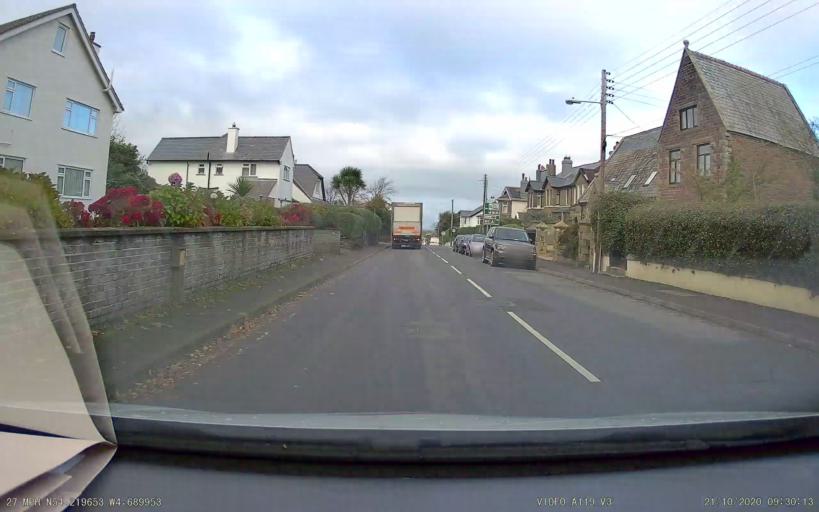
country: IM
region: Port Erin
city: Port Erin
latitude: 54.2196
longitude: -4.6899
